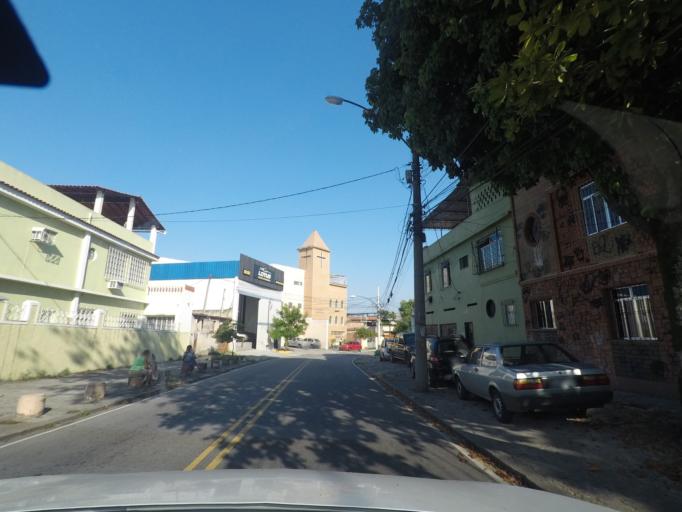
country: BR
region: Rio de Janeiro
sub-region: Duque De Caxias
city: Duque de Caxias
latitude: -22.8292
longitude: -43.2844
